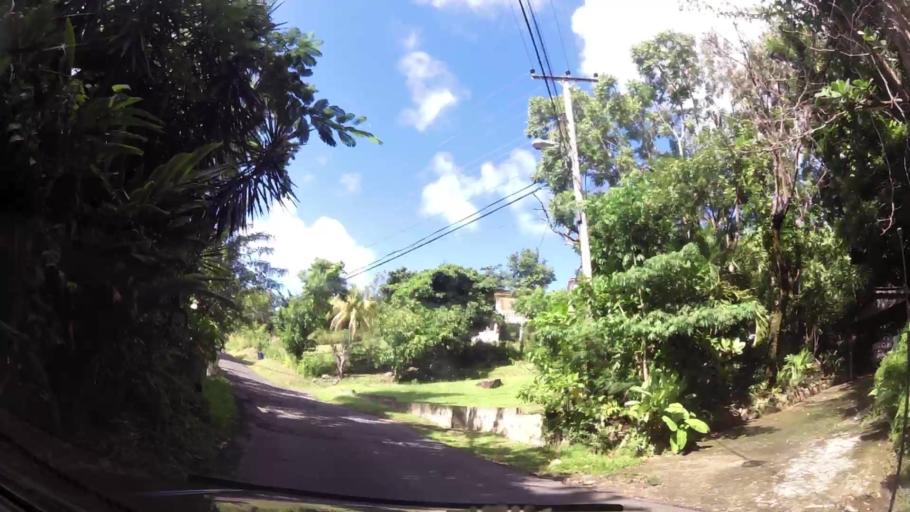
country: MS
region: Saint Peter
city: Saint Peters
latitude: 16.7531
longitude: -62.2219
